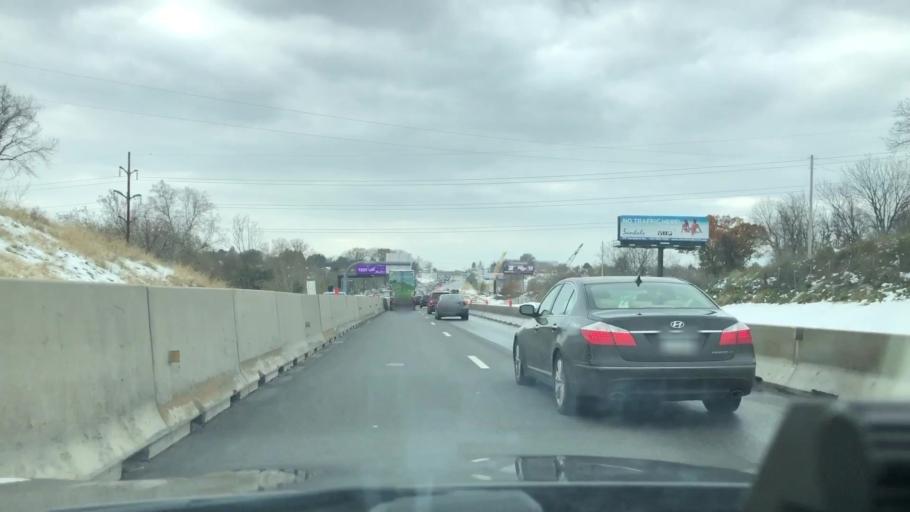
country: US
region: Pennsylvania
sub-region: Lehigh County
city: Fullerton
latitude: 40.6340
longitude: -75.4596
